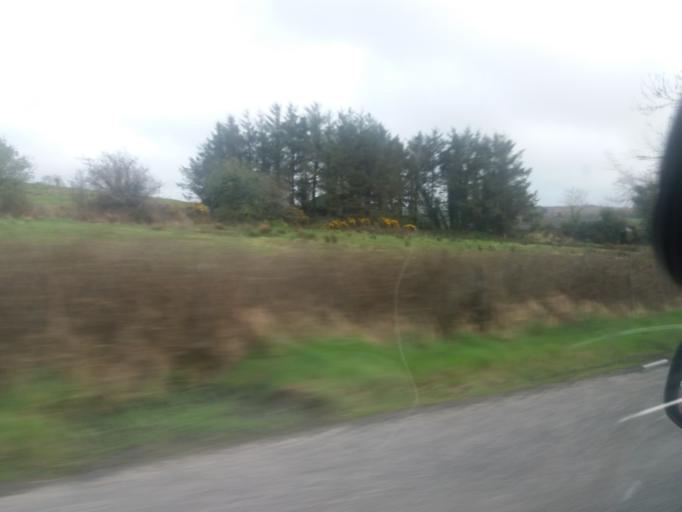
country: IE
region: Munster
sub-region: County Limerick
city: Newcastle West
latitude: 52.4033
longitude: -9.1693
